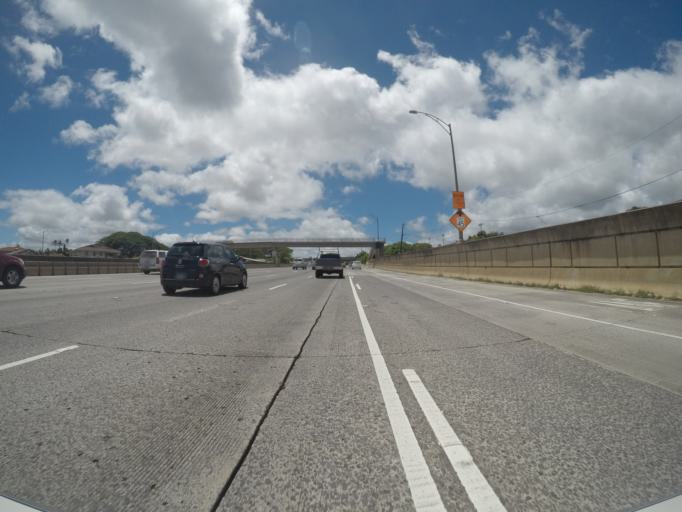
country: US
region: Hawaii
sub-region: Honolulu County
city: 'Aiea
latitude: 21.3821
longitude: -157.9306
